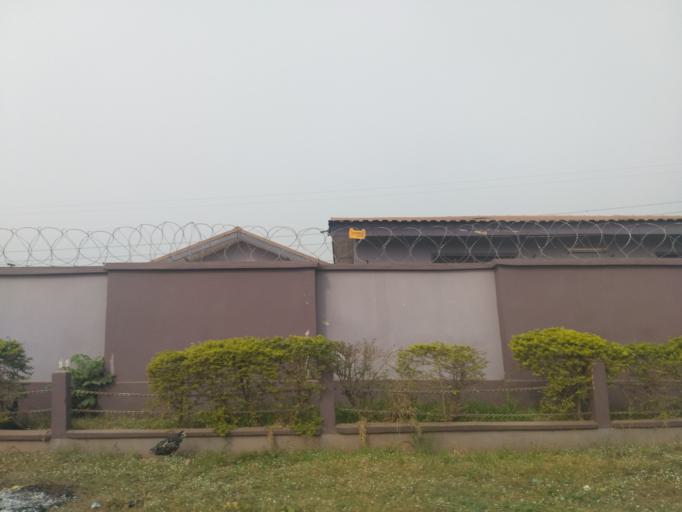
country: GH
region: Ashanti
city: Kumasi
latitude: 6.6629
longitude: -1.6141
